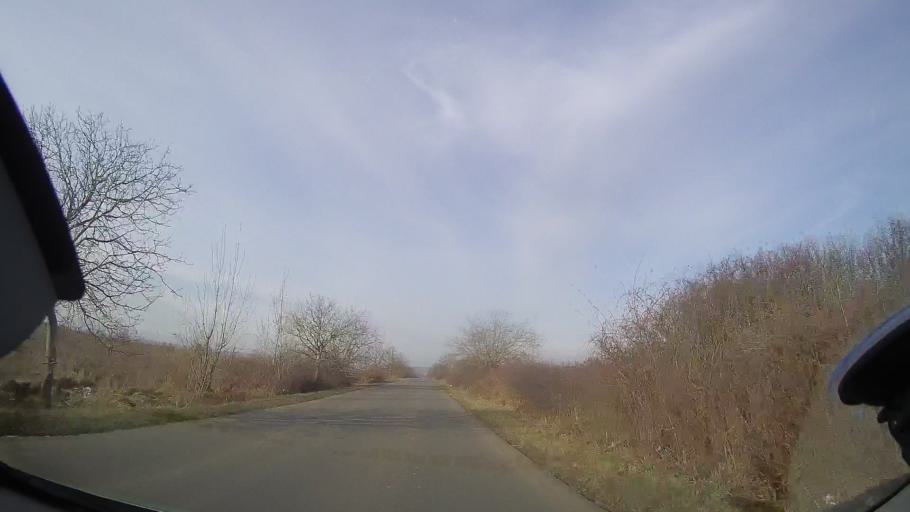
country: RO
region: Bihor
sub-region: Comuna Spinus
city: Spinus
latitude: 47.2221
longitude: 22.1707
